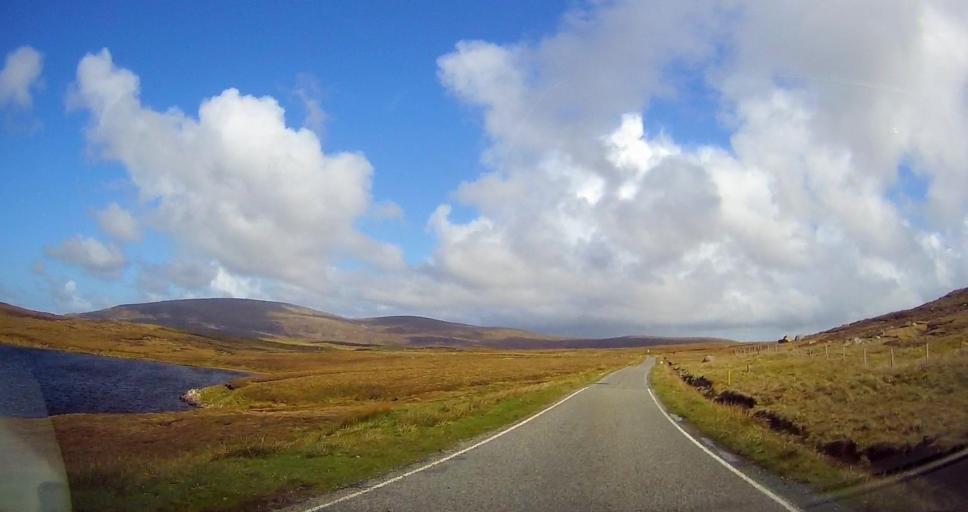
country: GB
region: Scotland
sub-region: Shetland Islands
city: Lerwick
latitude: 60.4930
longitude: -1.3916
